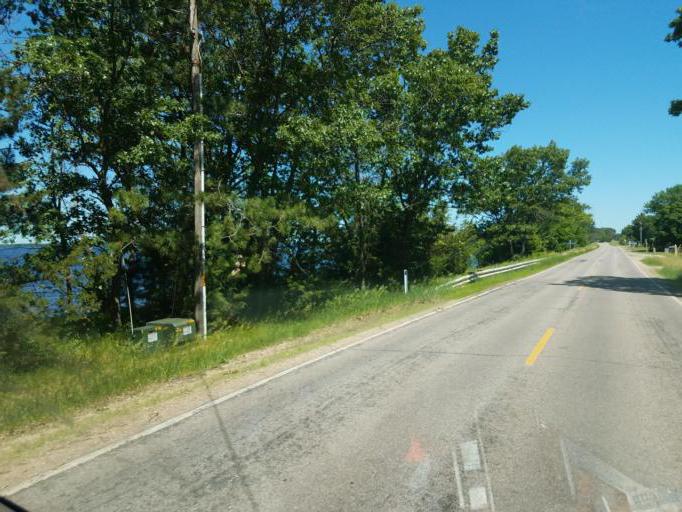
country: US
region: Wisconsin
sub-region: Adams County
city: Adams
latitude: 43.9127
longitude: -89.9378
